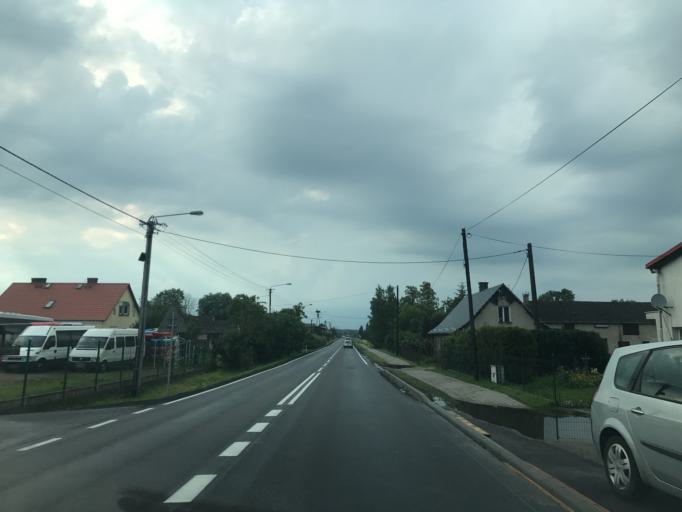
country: PL
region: Pomeranian Voivodeship
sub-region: Powiat czluchowski
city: Czluchow
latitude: 53.6754
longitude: 17.3445
